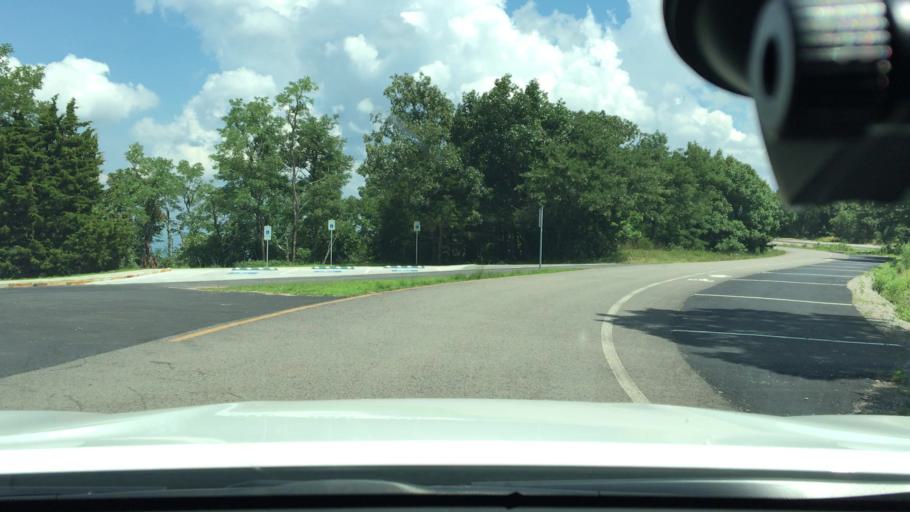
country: US
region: Arkansas
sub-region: Logan County
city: Paris
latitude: 35.1733
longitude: -93.6468
